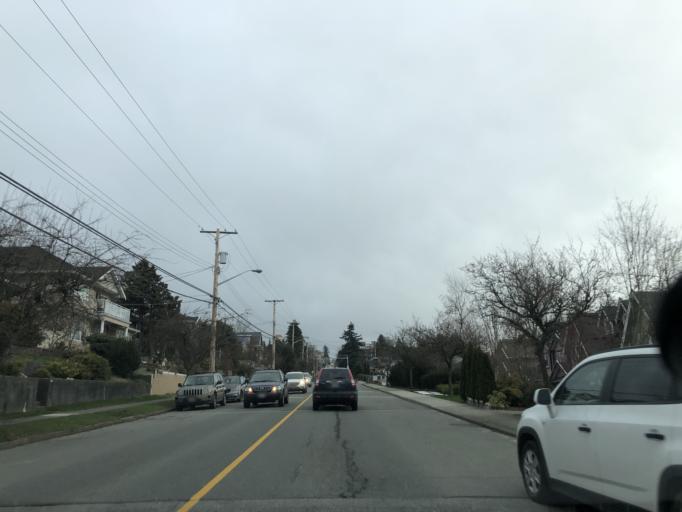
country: CA
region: British Columbia
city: New Westminster
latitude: 49.2047
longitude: -122.9358
